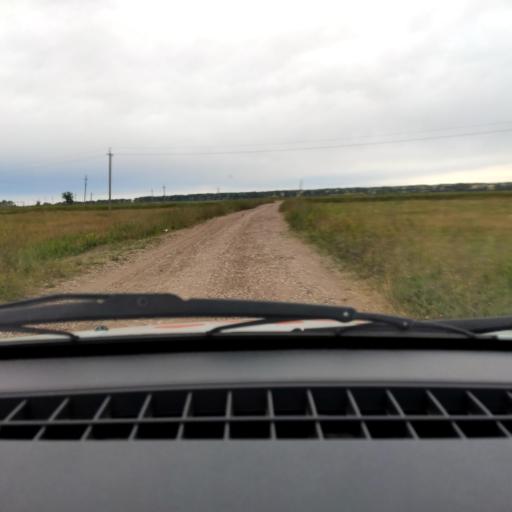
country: RU
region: Bashkortostan
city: Avdon
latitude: 54.5081
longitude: 55.7909
